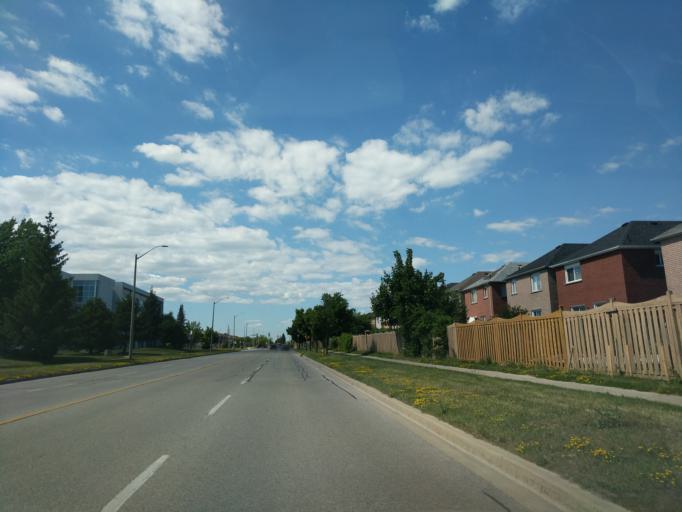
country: CA
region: Ontario
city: Markham
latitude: 43.8460
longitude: -79.2661
